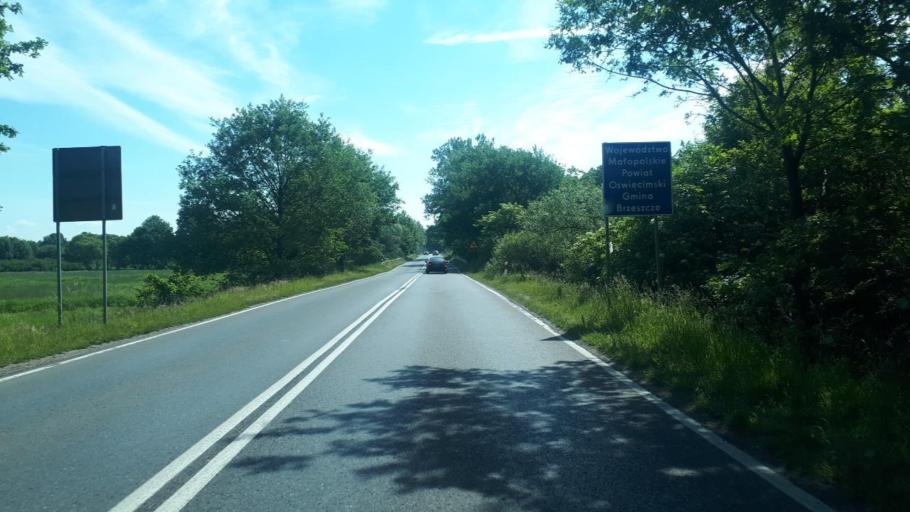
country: PL
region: Silesian Voivodeship
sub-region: Powiat pszczynski
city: Gora
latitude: 49.9732
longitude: 19.1116
